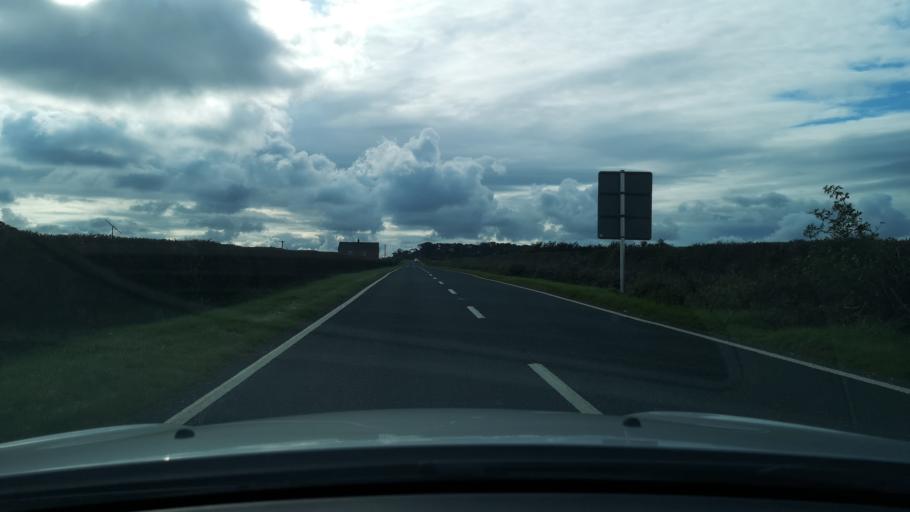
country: GB
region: England
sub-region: East Riding of Yorkshire
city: Walkington
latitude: 53.8117
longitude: -0.5307
